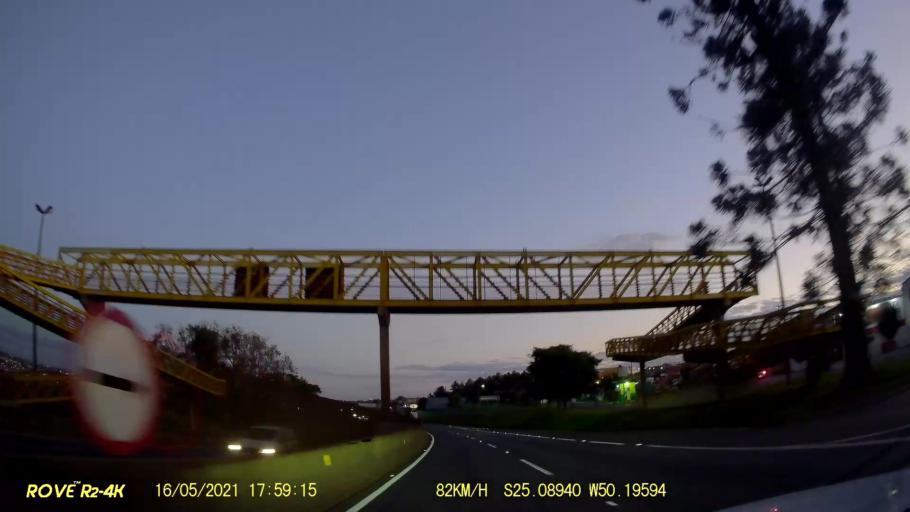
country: BR
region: Parana
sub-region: Ponta Grossa
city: Ponta Grossa
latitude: -25.0893
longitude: -50.1959
